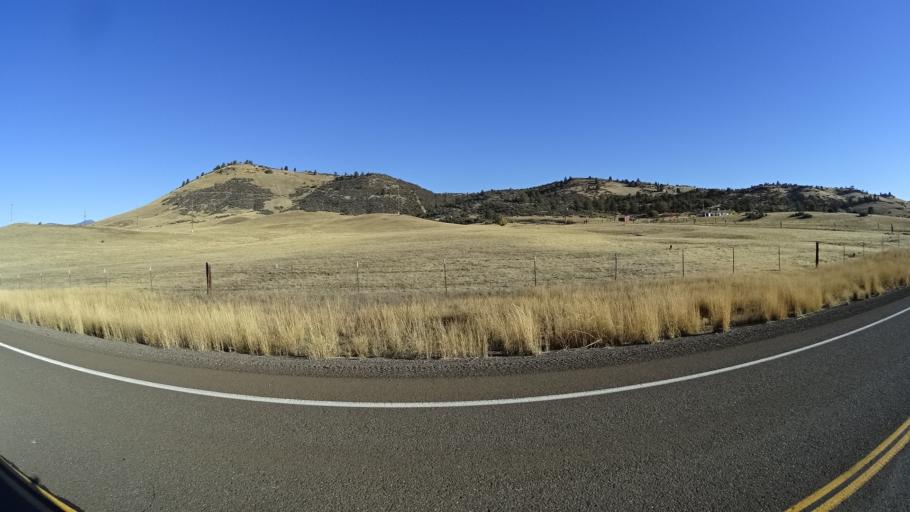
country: US
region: California
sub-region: Siskiyou County
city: Montague
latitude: 41.8977
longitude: -122.5371
